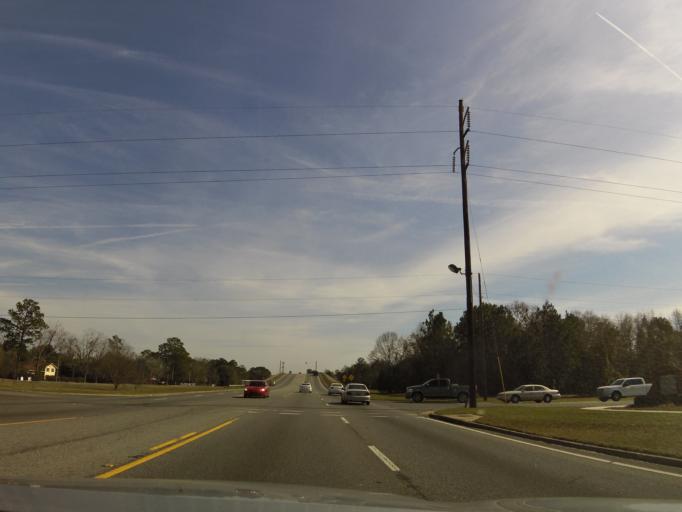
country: US
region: Georgia
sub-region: Ware County
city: Waycross
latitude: 31.2087
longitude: -82.3729
